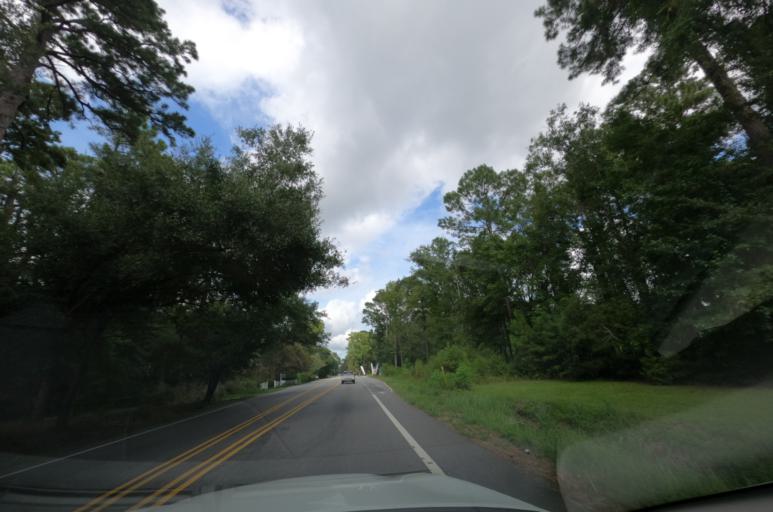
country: US
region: South Carolina
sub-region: Charleston County
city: Shell Point
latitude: 32.7385
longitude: -80.0478
